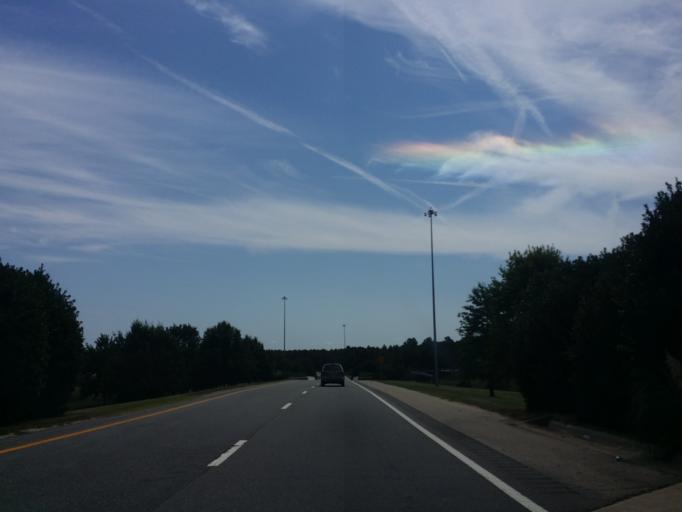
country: US
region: North Carolina
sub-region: Wake County
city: Morrisville
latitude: 35.8664
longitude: -78.8051
